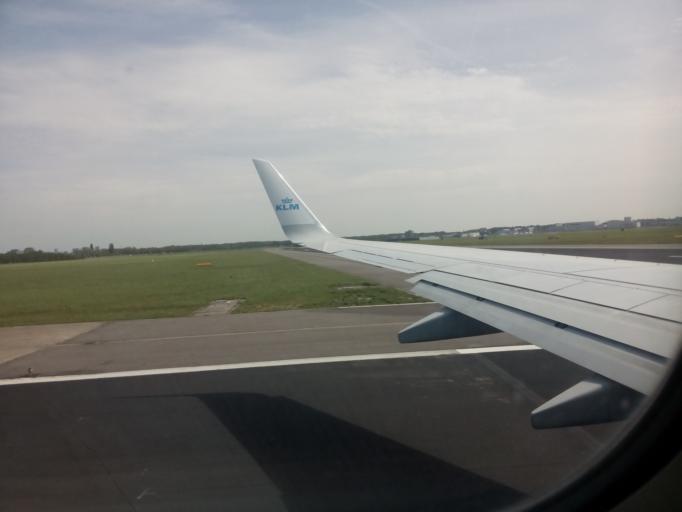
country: NL
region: North Holland
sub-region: Gemeente Aalsmeer
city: Aalsmeer
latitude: 52.3194
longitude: 4.7800
